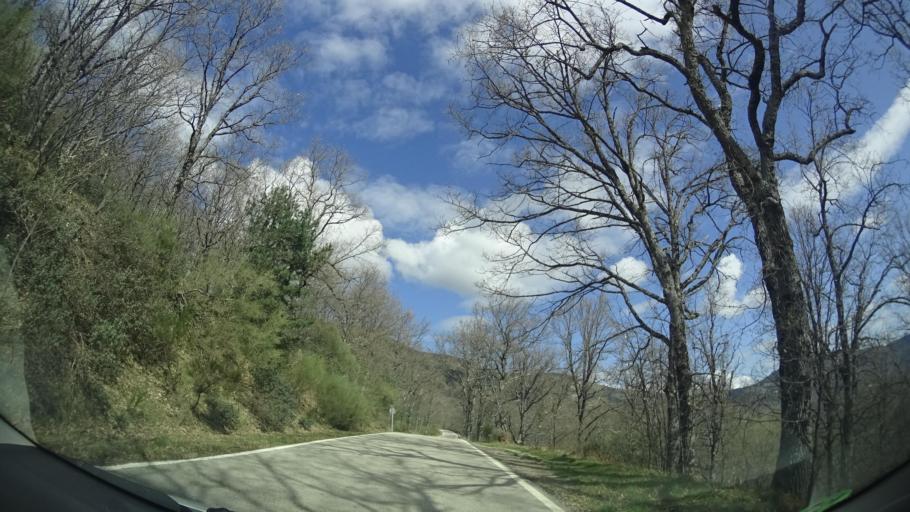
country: ES
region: Madrid
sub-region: Provincia de Madrid
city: Miraflores de la Sierra
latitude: 40.8269
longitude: -3.7642
